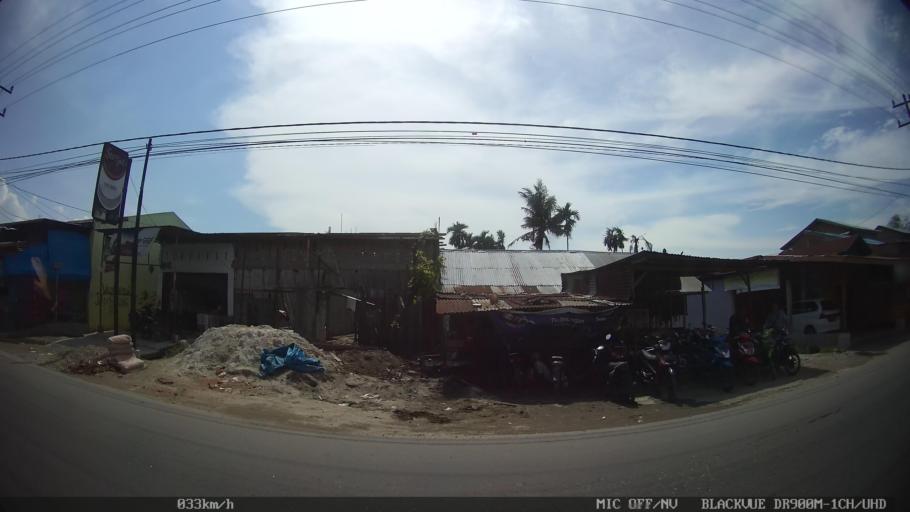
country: ID
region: North Sumatra
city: Labuhan Deli
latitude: 3.6612
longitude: 98.6564
